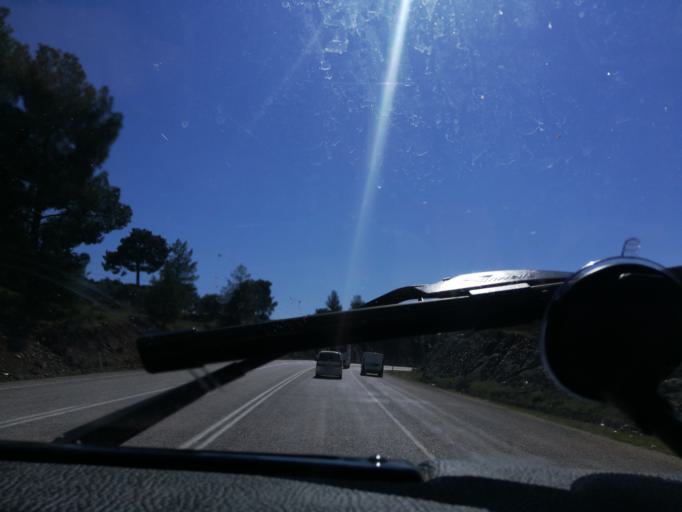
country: TR
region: Mugla
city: Kemer
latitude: 36.6103
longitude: 29.3584
